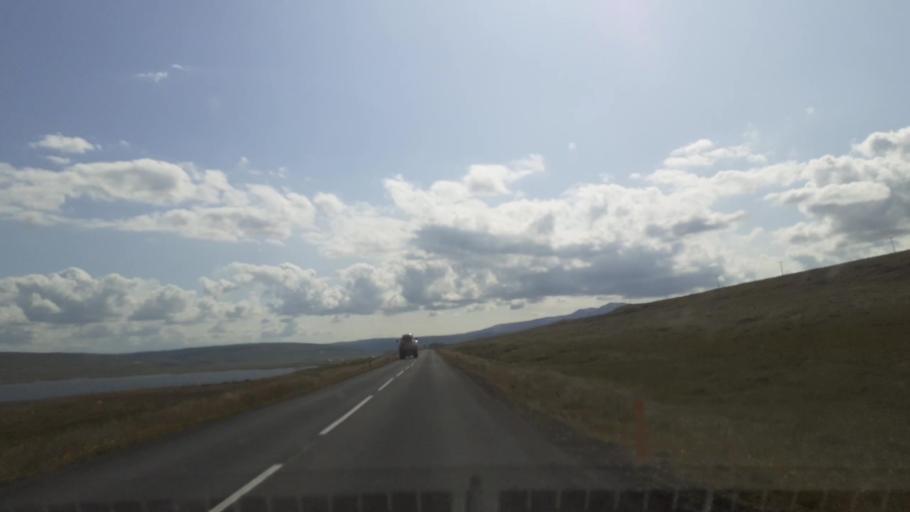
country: IS
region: West
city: Borgarnes
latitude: 65.1716
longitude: -21.0959
